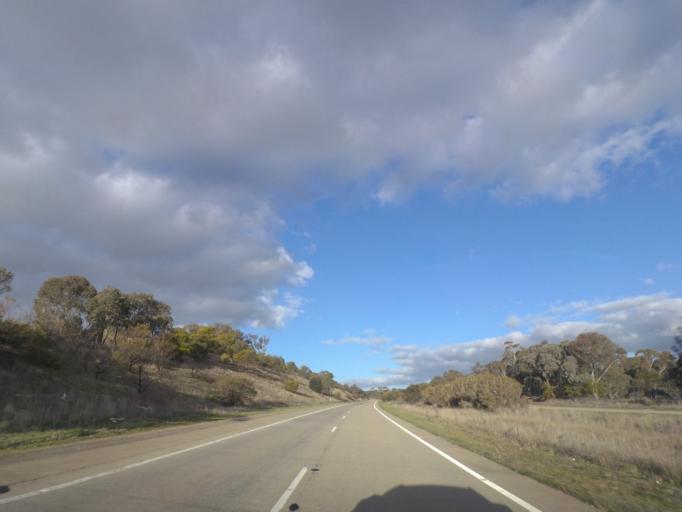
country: AU
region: New South Wales
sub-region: Yass Valley
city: Yass
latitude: -34.7998
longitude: 148.5368
